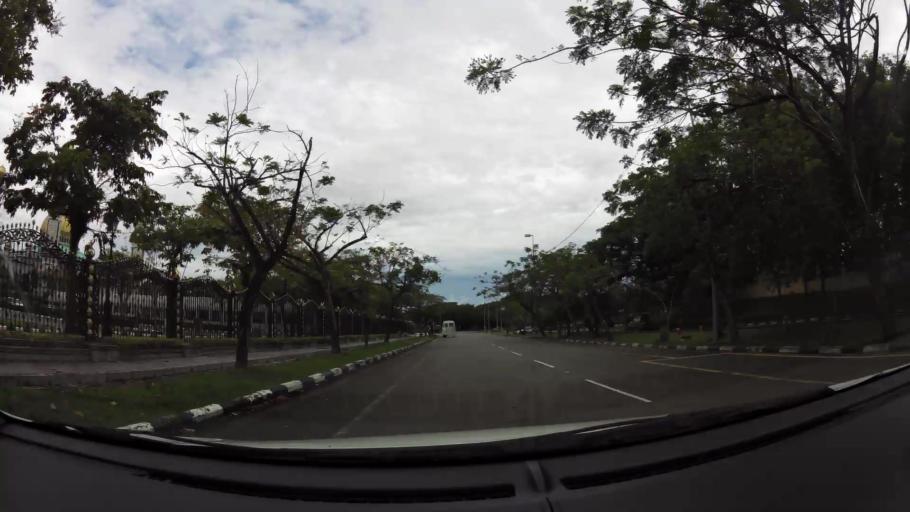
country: BN
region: Brunei and Muara
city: Bandar Seri Begawan
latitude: 4.8990
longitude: 114.9230
